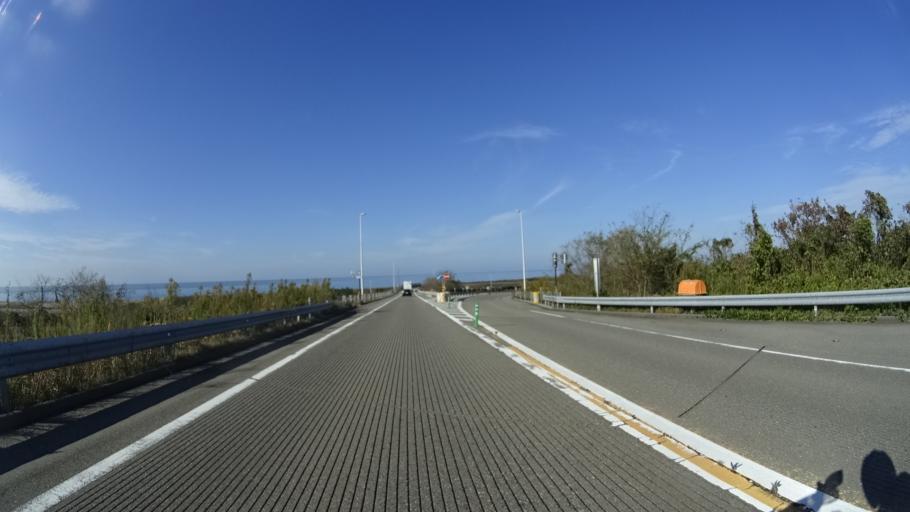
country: JP
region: Ishikawa
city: Kanazawa-shi
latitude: 36.6490
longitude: 136.6358
